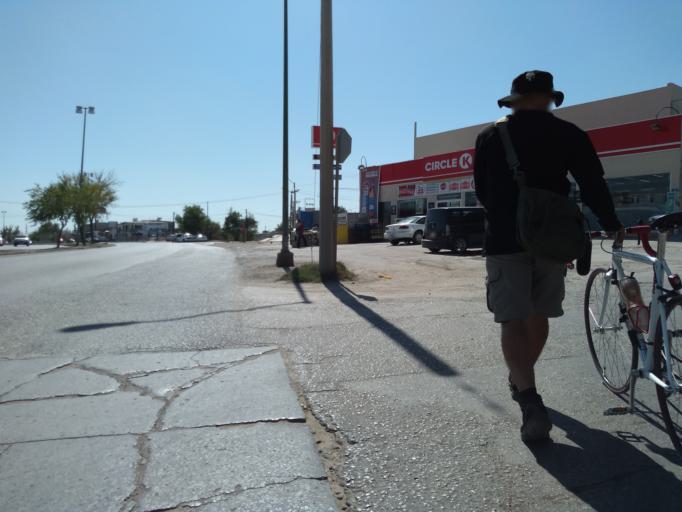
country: US
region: Texas
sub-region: El Paso County
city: El Paso
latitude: 31.7512
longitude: -106.4969
